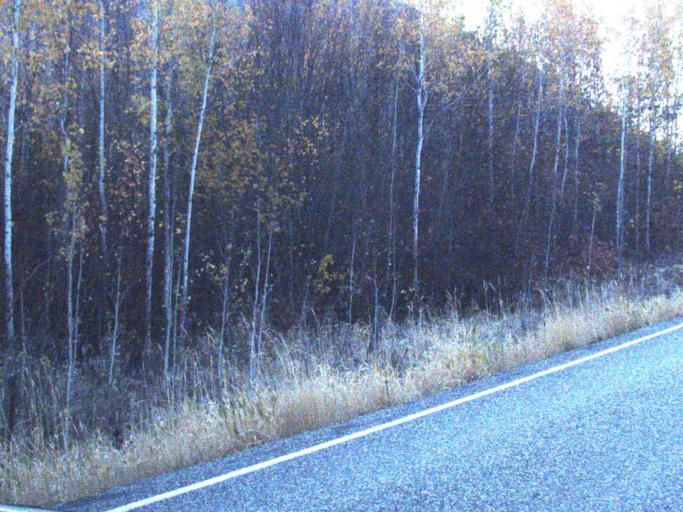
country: US
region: Washington
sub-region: Okanogan County
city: Coulee Dam
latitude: 48.2195
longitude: -118.7074
